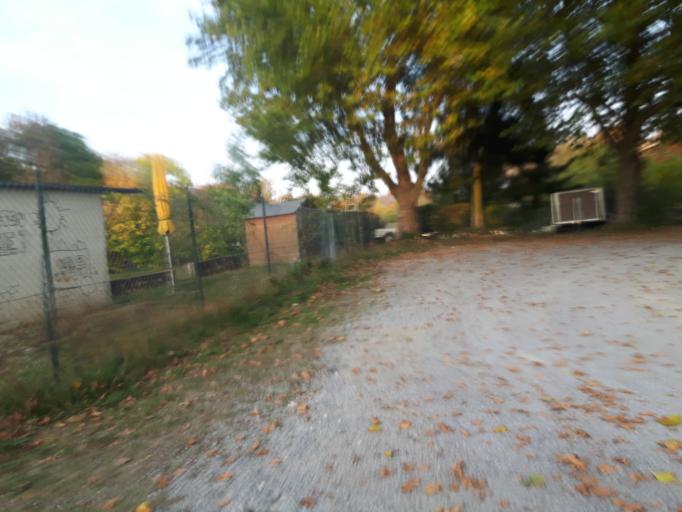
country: DE
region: Baden-Wuerttemberg
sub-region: Regierungsbezirk Stuttgart
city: Lauffen am Neckar
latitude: 49.0773
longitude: 9.1583
